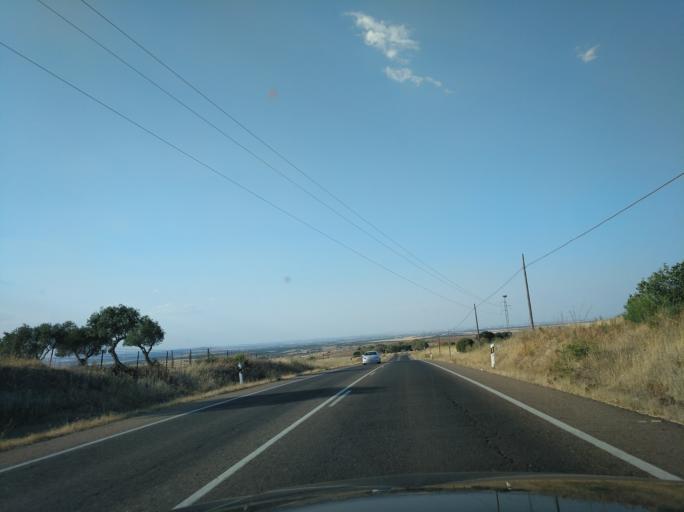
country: ES
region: Extremadura
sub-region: Provincia de Badajoz
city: Olivenza
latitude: 38.7149
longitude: -7.0849
